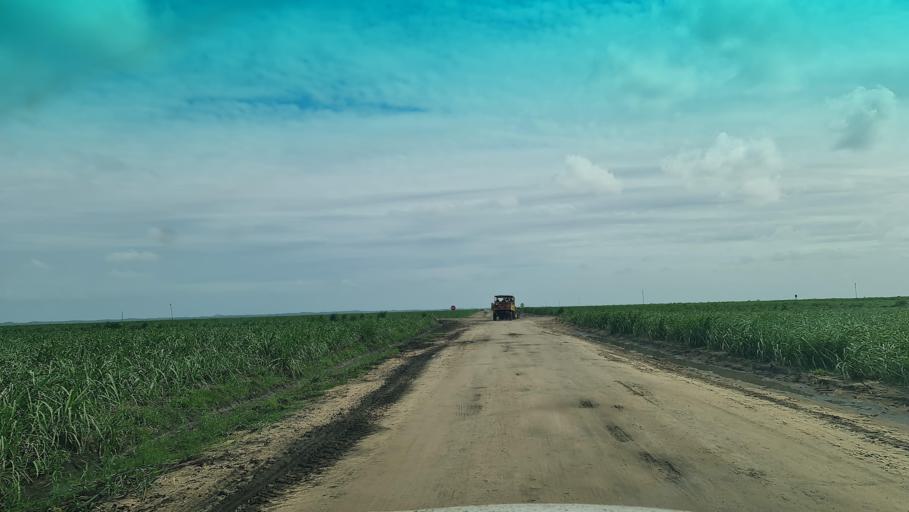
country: MZ
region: Maputo
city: Manhica
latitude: -25.4767
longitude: 32.8166
